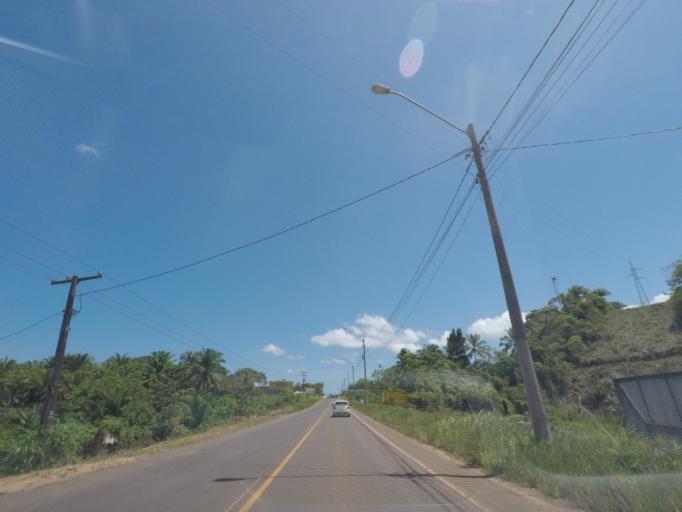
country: BR
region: Bahia
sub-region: Valenca
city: Valenca
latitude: -13.3452
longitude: -39.0628
